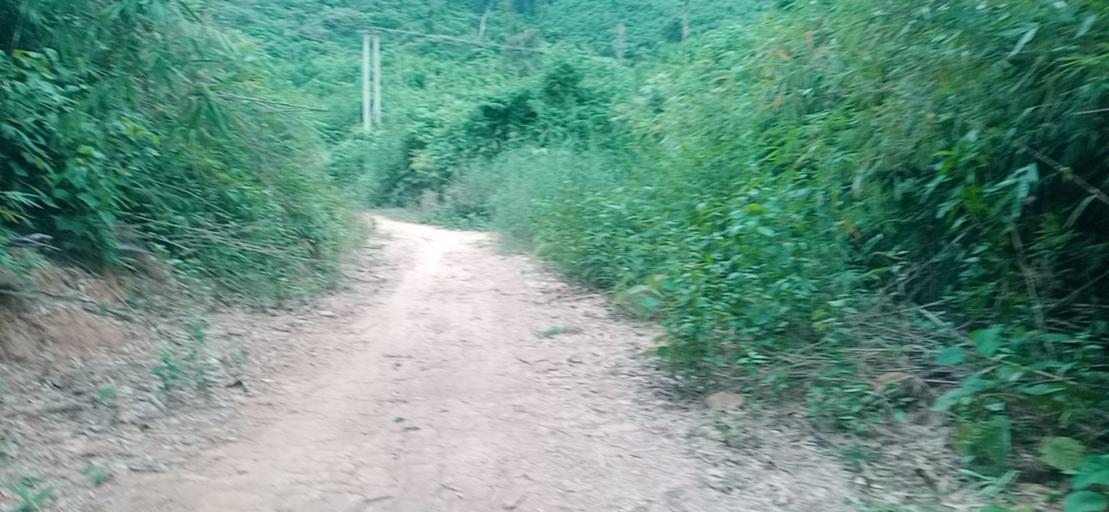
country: TH
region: Changwat Bueng Kan
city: Pak Khat
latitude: 18.5595
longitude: 103.2416
